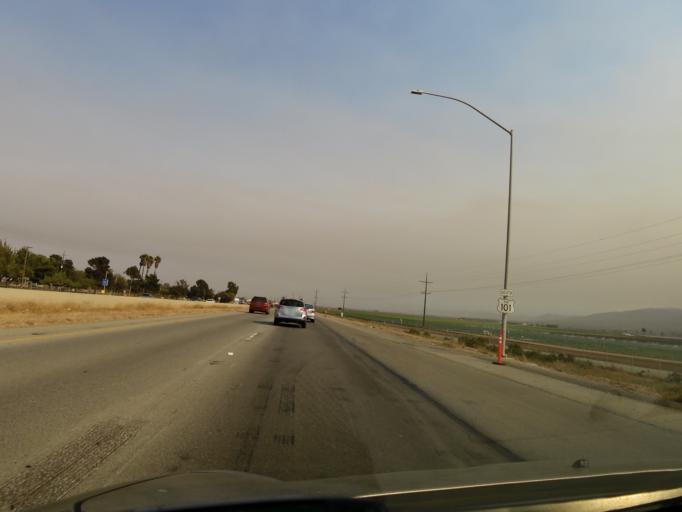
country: US
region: California
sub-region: Monterey County
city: Soledad
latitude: 36.4617
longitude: -121.3835
